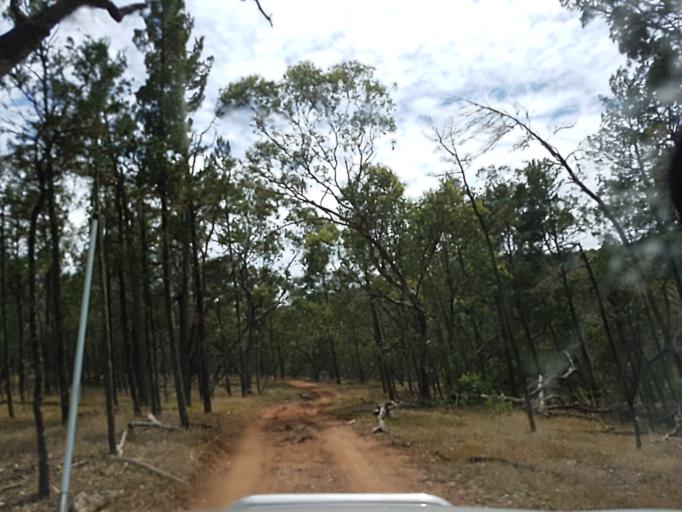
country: AU
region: New South Wales
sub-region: Snowy River
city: Jindabyne
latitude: -36.9388
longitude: 148.3990
